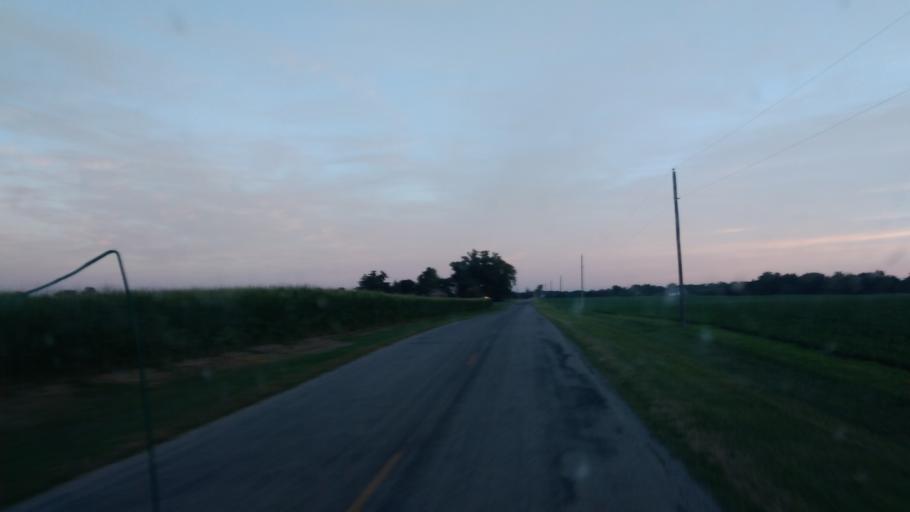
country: US
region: Indiana
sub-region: Wells County
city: Bluffton
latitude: 40.6756
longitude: -85.1304
